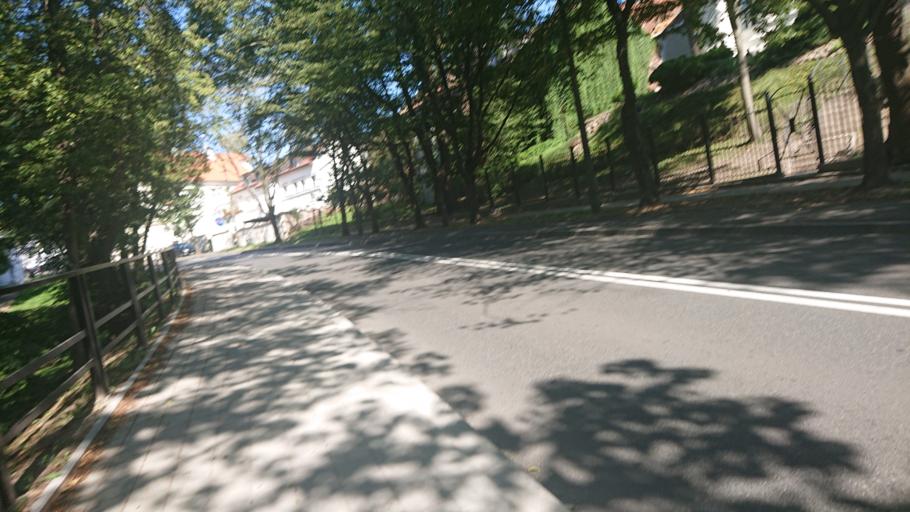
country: PL
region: Masovian Voivodeship
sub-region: Plock
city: Plock
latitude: 52.5415
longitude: 19.6907
